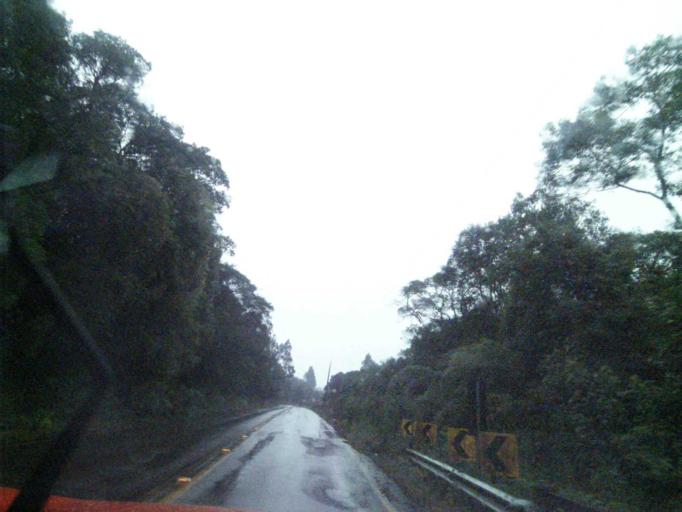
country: BR
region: Santa Catarina
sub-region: Anitapolis
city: Anitapolis
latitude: -27.7796
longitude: -49.0421
